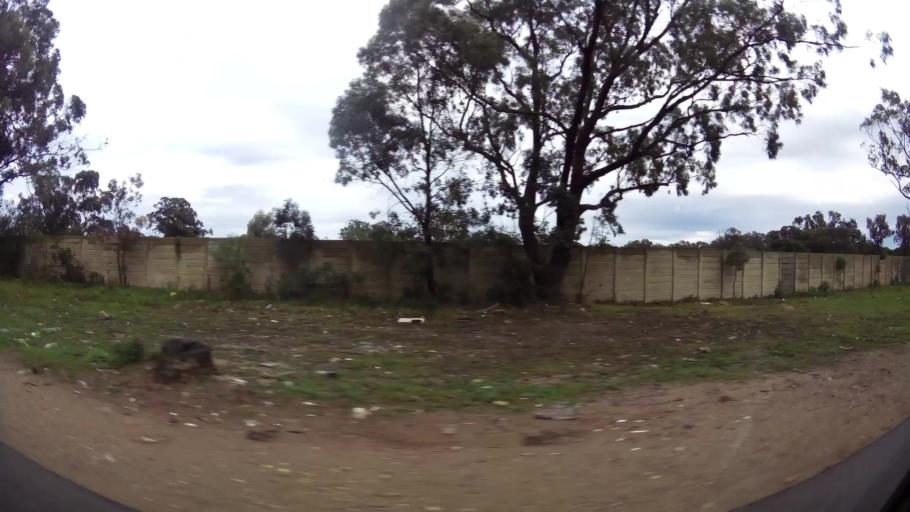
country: ZA
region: Eastern Cape
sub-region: Nelson Mandela Bay Metropolitan Municipality
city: Port Elizabeth
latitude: -33.9957
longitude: 25.5784
